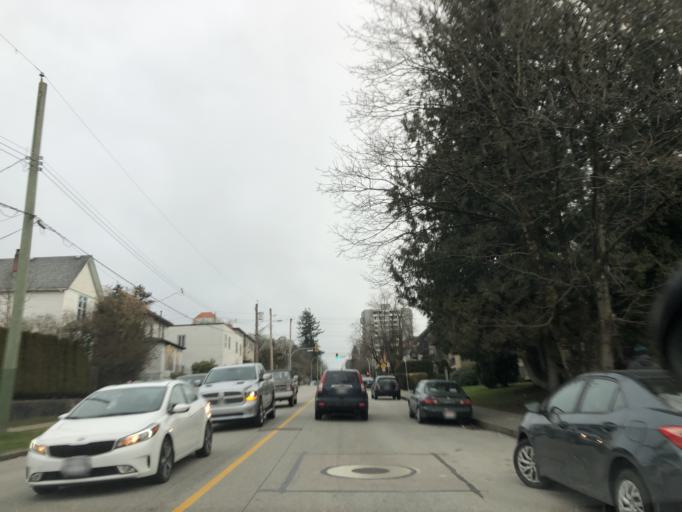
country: CA
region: British Columbia
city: New Westminster
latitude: 49.2089
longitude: -122.9282
